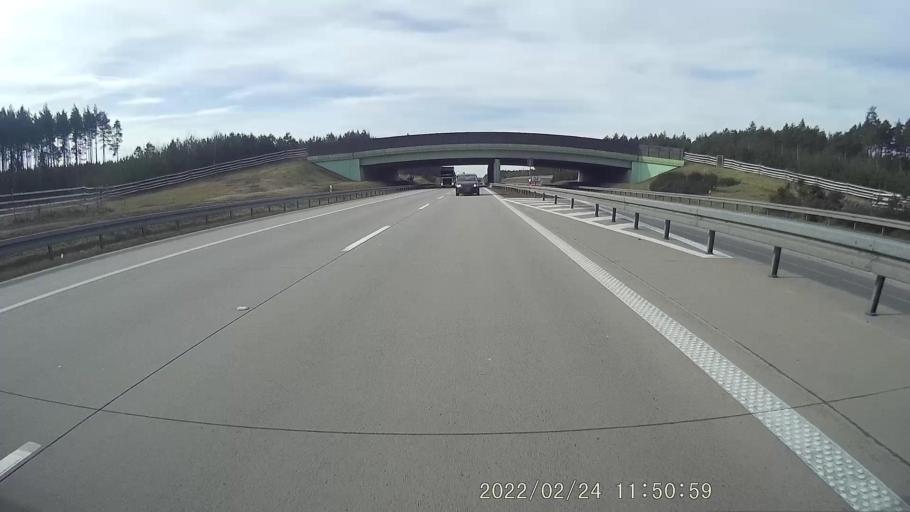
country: PL
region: Lower Silesian Voivodeship
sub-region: Powiat polkowicki
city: Radwanice
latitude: 51.6067
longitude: 15.9668
